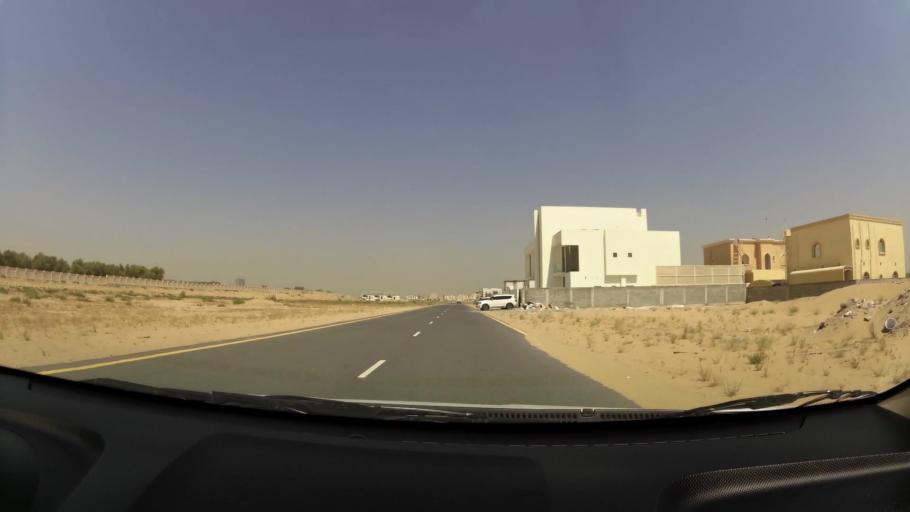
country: AE
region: Ajman
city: Ajman
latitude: 25.4033
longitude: 55.5349
